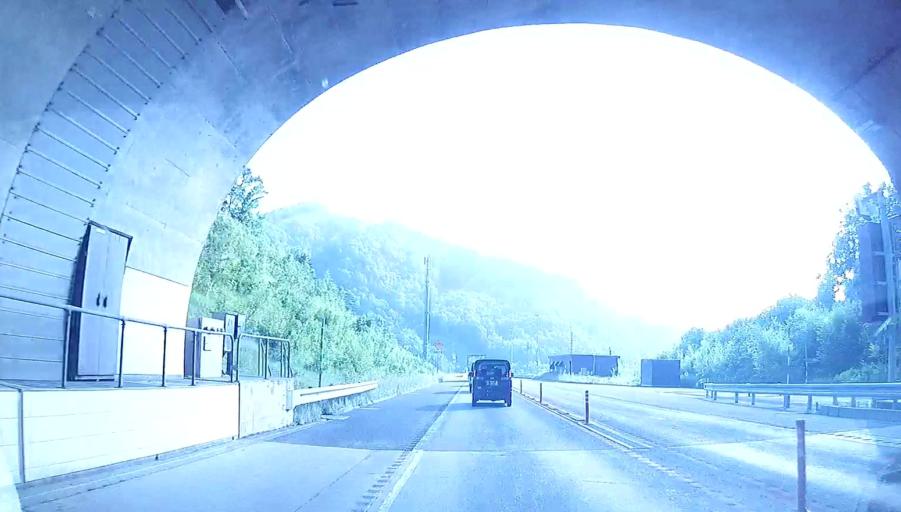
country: JP
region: Hokkaido
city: Shimo-furano
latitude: 43.0533
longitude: 142.4992
